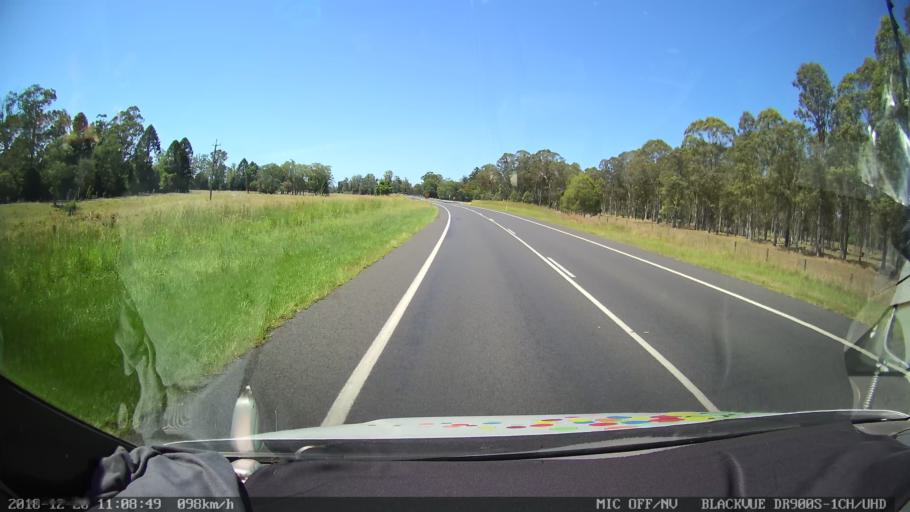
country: AU
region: New South Wales
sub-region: Richmond Valley
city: Casino
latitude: -28.9272
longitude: 153.0046
